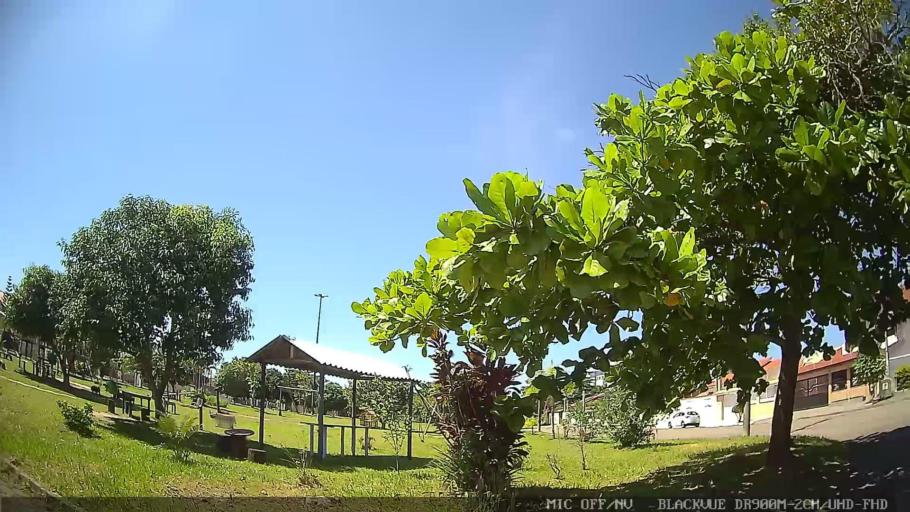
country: BR
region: Sao Paulo
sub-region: Peruibe
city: Peruibe
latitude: -24.3042
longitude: -46.9856
